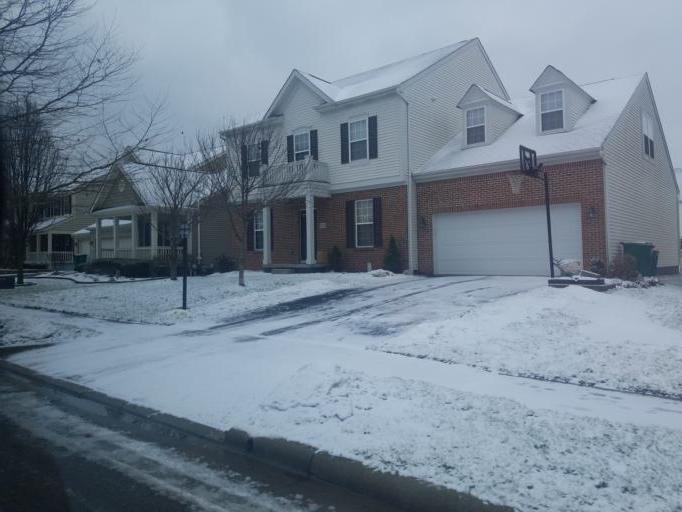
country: US
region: Ohio
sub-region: Franklin County
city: Reynoldsburg
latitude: 40.0164
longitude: -82.7947
